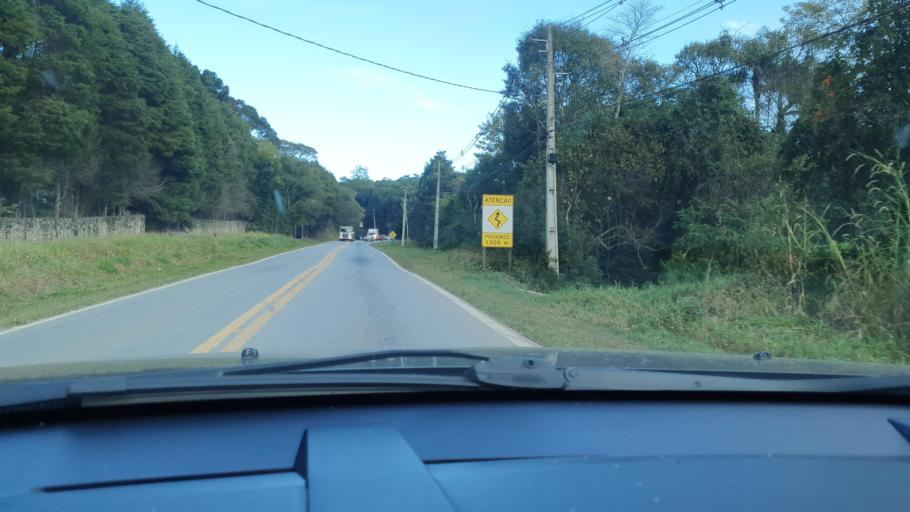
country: BR
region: Sao Paulo
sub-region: Ibiuna
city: Ibiuna
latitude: -23.6768
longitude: -47.2943
